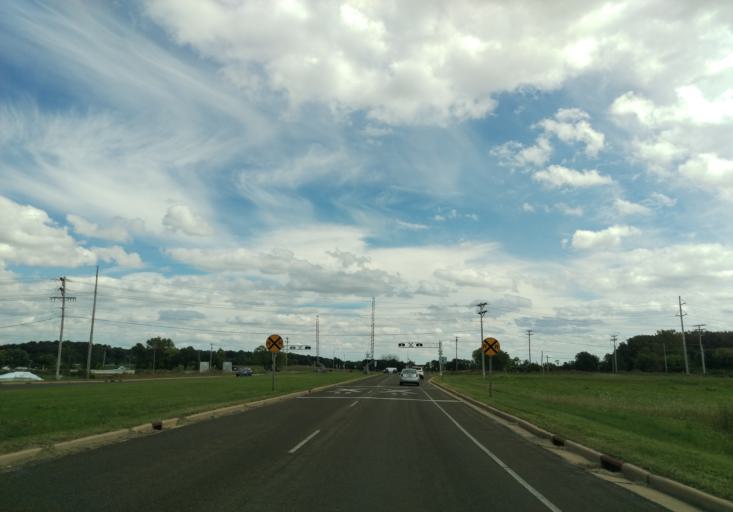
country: US
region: Wisconsin
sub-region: Dane County
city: Maple Bluff
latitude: 43.1532
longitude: -89.4075
